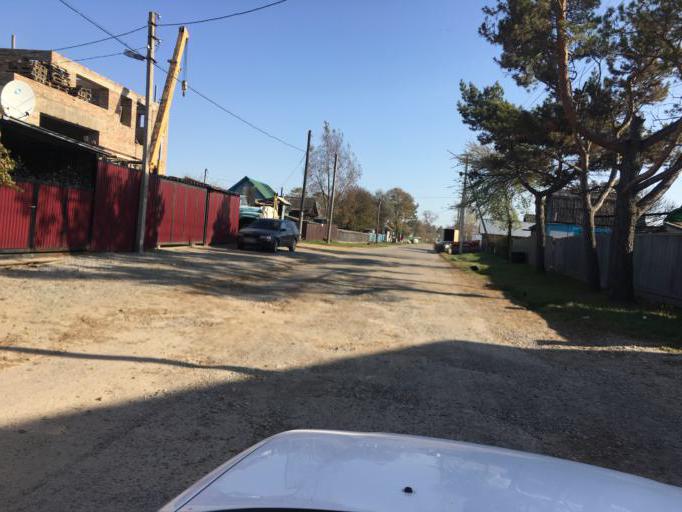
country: RU
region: Primorskiy
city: Dal'nerechensk
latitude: 45.9259
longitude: 133.7221
